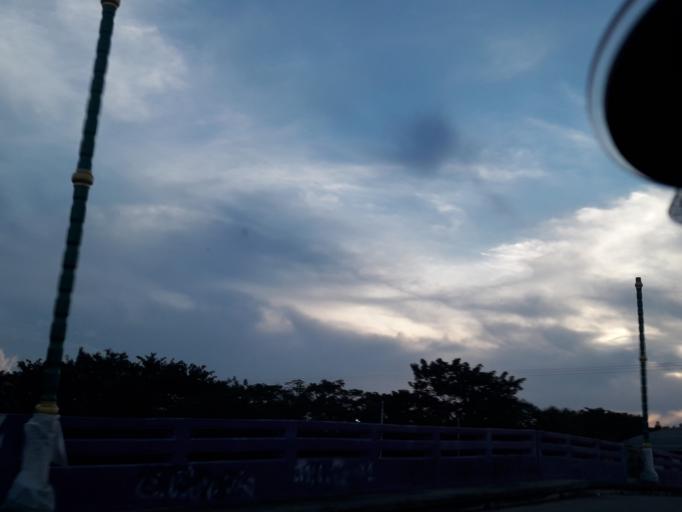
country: TH
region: Pathum Thani
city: Nong Suea
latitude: 14.1181
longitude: 100.8689
